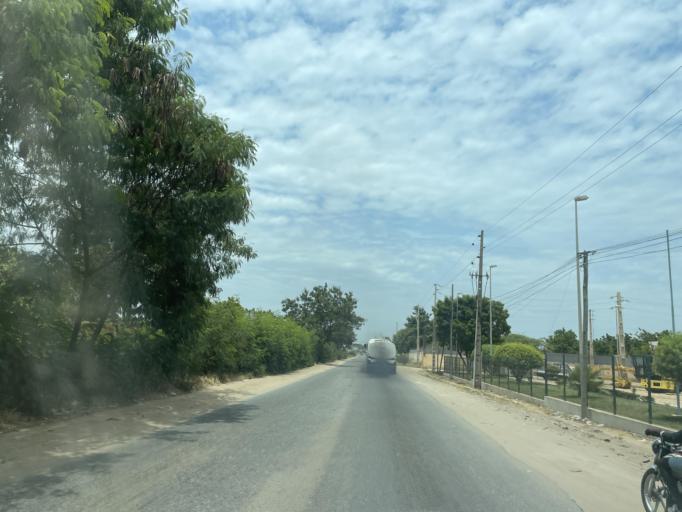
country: AO
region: Luanda
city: Luanda
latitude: -8.9362
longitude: 13.3905
